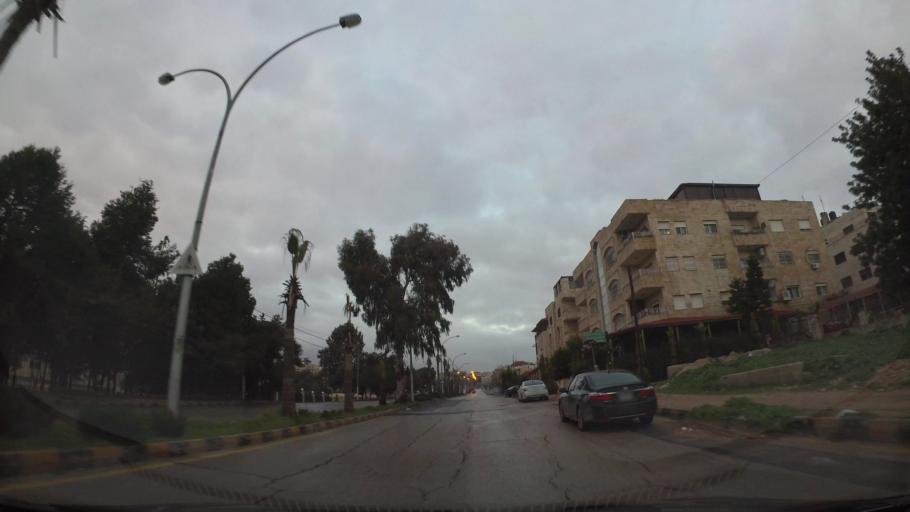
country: JO
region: Amman
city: Amman
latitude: 31.9849
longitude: 35.9105
